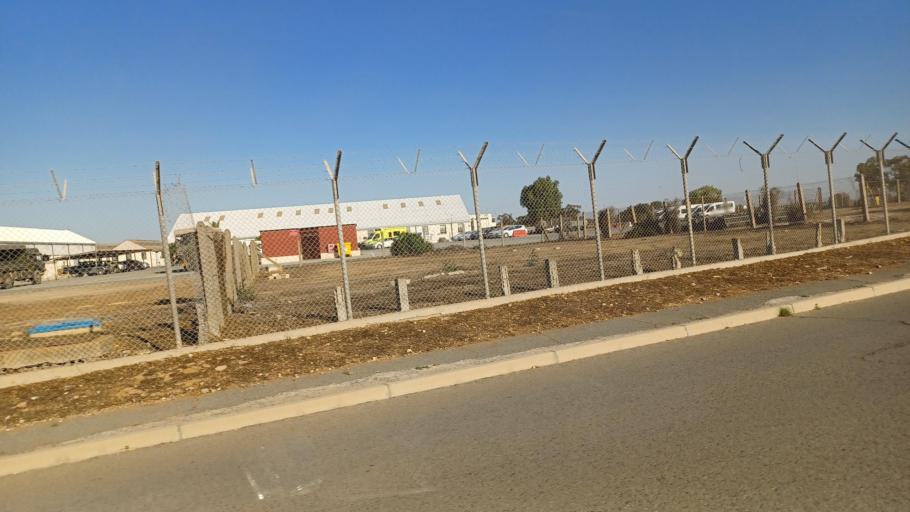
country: CY
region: Larnaka
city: Xylotymbou
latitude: 34.9995
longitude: 33.7426
